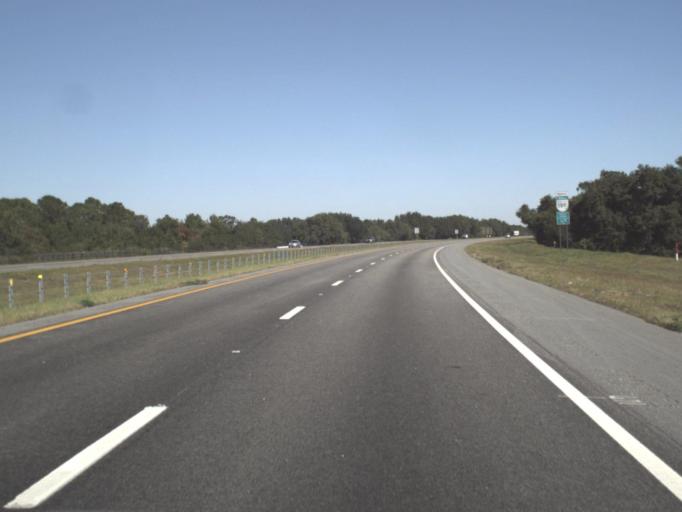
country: US
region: Florida
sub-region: Pasco County
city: Shady Hills
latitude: 28.3392
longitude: -82.5509
